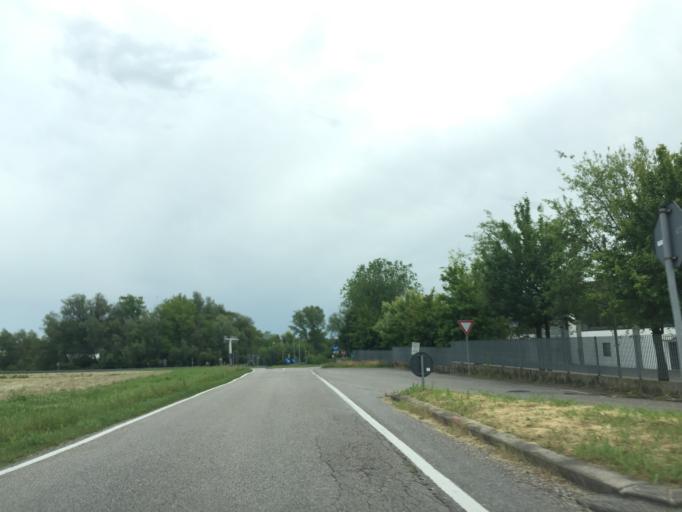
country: IT
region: Friuli Venezia Giulia
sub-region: Provincia di Pordenone
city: Porcia
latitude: 45.9581
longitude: 12.5823
